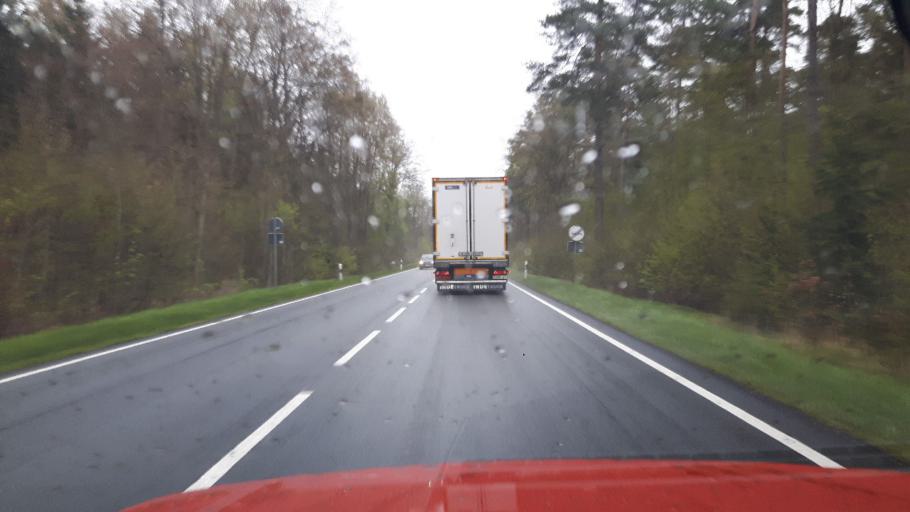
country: DE
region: Bavaria
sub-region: Regierungsbezirk Mittelfranken
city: Muhr am See
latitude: 49.1672
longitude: 10.7169
